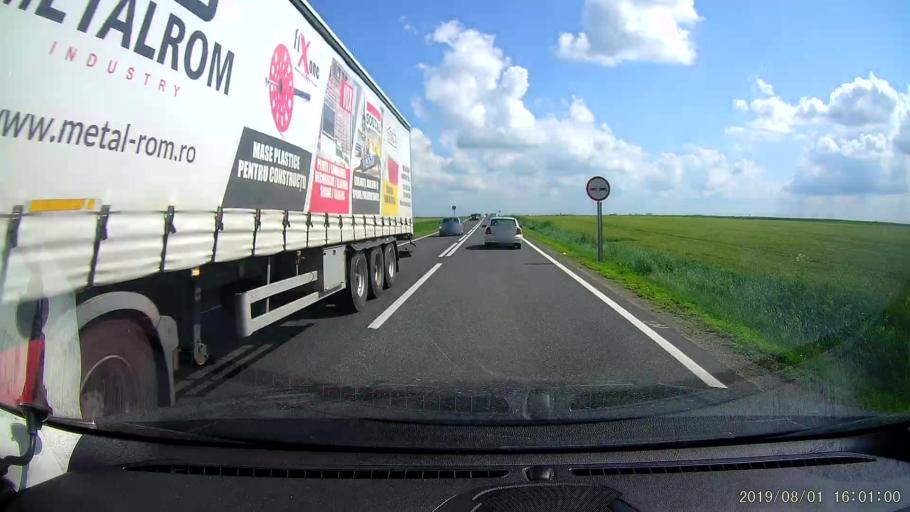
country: RO
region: Ialomita
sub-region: Comuna Ciulnita
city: Ciulnita
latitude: 44.5161
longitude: 27.3898
